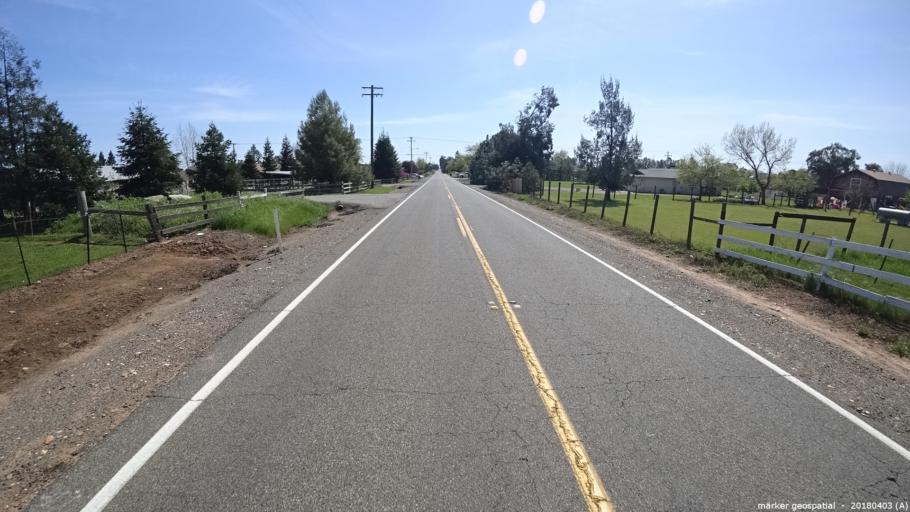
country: US
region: California
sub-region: Sacramento County
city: Herald
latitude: 38.3515
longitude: -121.2238
